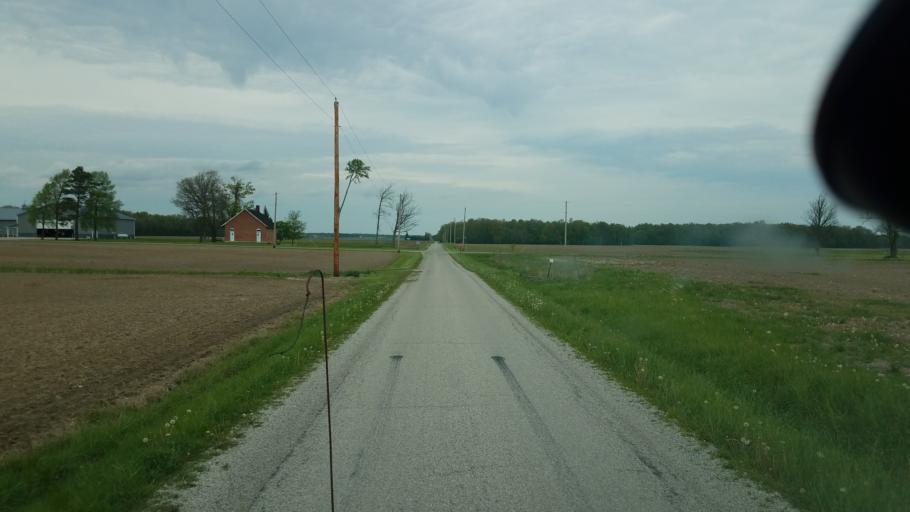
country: US
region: Ohio
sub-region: Huron County
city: Willard
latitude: 41.0285
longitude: -82.8619
